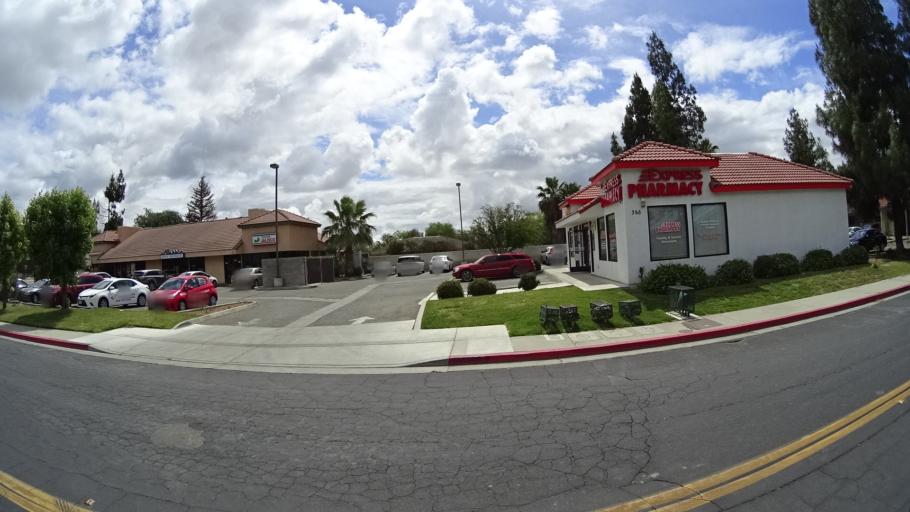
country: US
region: California
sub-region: Kings County
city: Hanford
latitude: 36.3277
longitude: -119.6631
